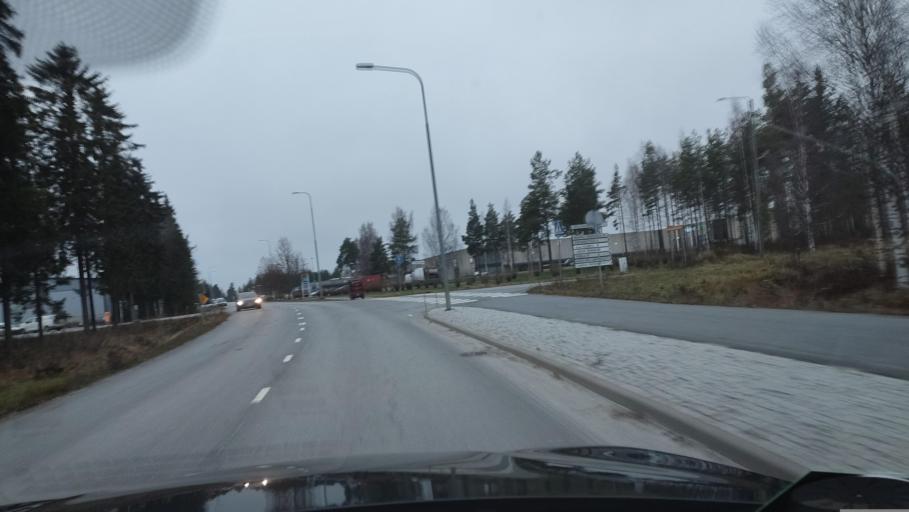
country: FI
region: Southern Ostrobothnia
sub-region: Suupohja
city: Kauhajoki
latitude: 62.4583
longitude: 22.2070
